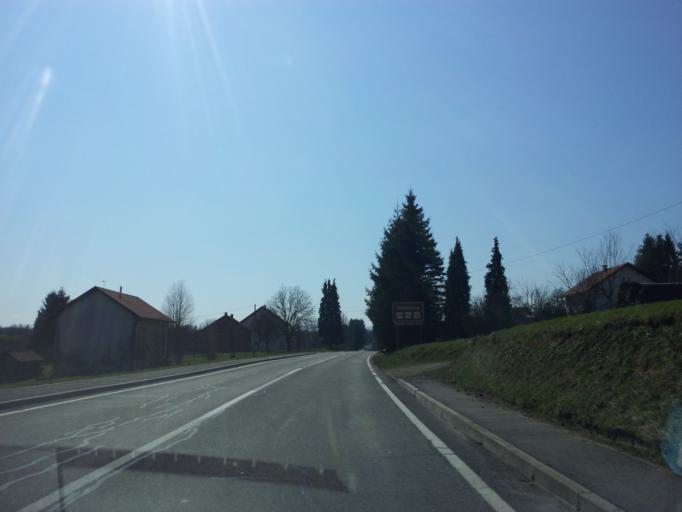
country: HR
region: Licko-Senjska
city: Jezerce
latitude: 45.0000
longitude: 15.6517
